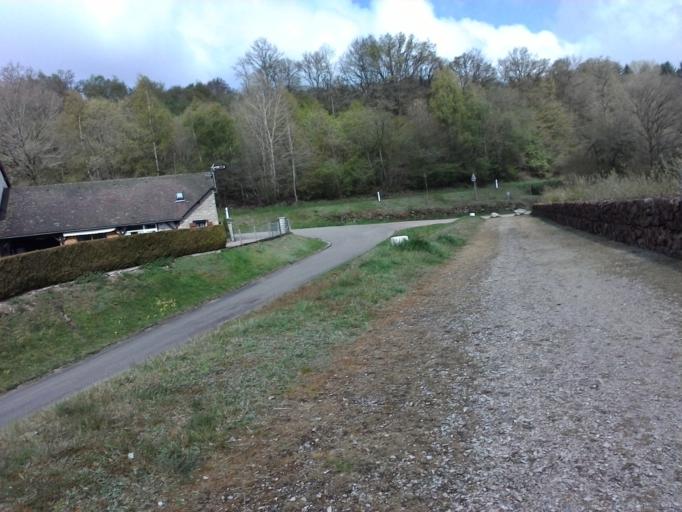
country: FR
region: Bourgogne
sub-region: Departement de la Cote-d'Or
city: Saulieu
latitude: 47.2452
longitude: 4.1879
